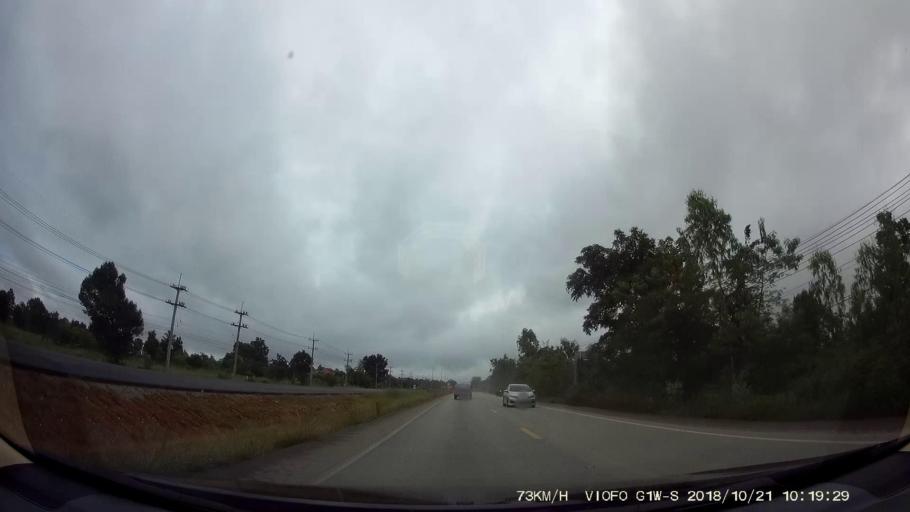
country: TH
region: Chaiyaphum
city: Phu Khiao
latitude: 16.3140
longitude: 102.1988
